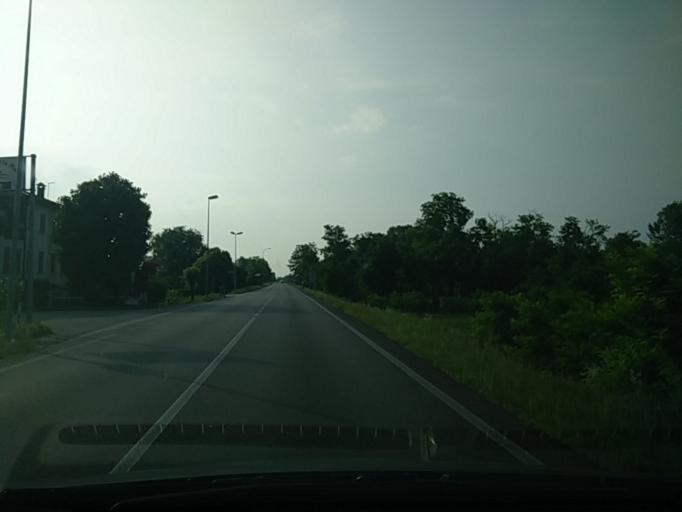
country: IT
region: Veneto
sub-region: Provincia di Venezia
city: San Dona di Piave
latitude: 45.6160
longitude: 12.5763
